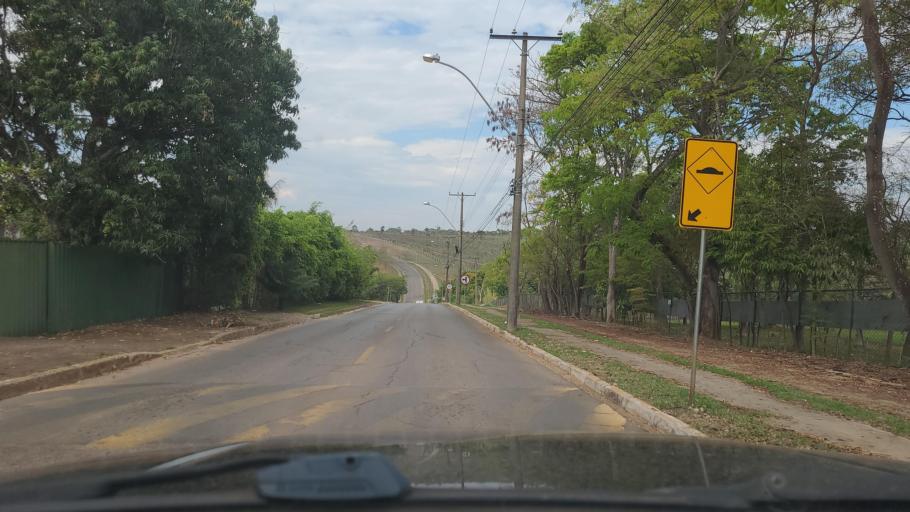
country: BR
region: Federal District
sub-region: Brasilia
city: Brasilia
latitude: -15.8595
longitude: -47.8580
